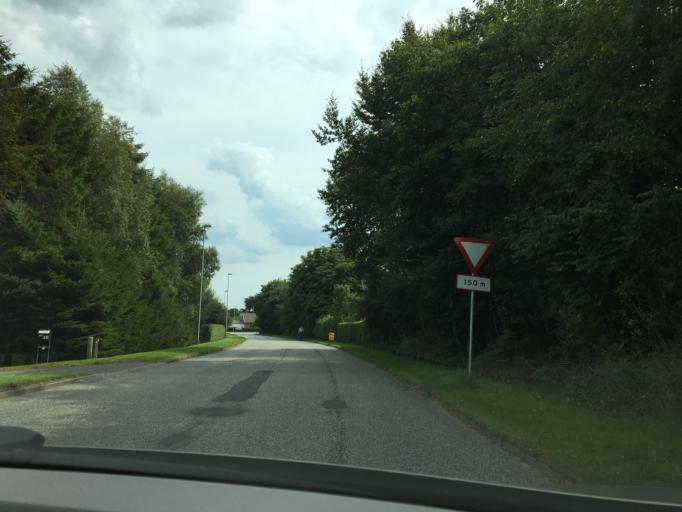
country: DK
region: Central Jutland
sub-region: Viborg Kommune
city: Stoholm
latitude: 56.4891
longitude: 9.1402
